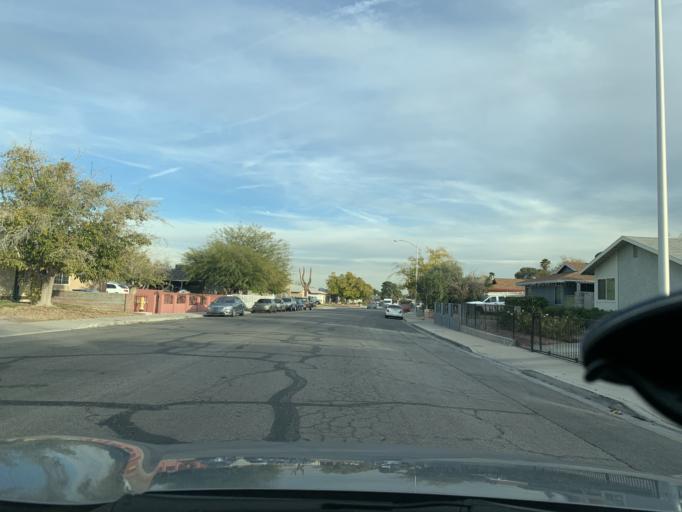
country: US
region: Nevada
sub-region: Clark County
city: Spring Valley
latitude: 36.0970
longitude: -115.2303
